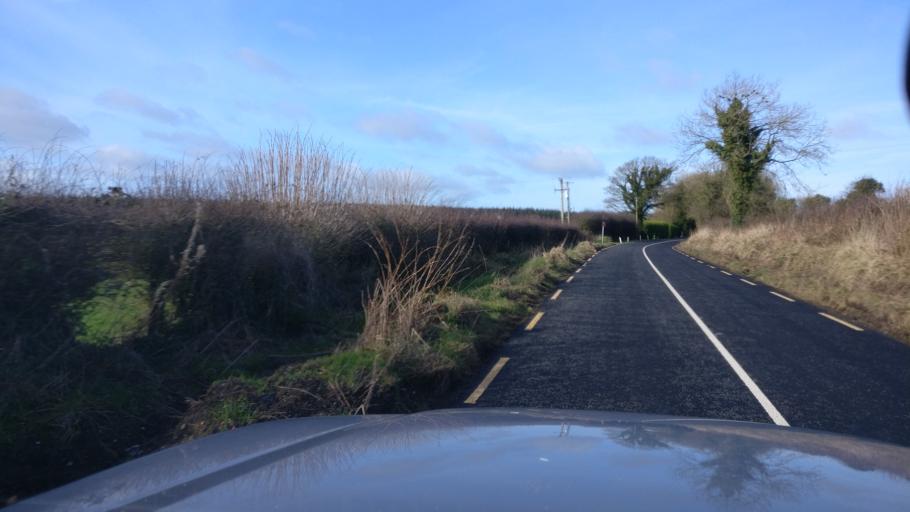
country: IE
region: Leinster
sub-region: Kilkenny
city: Castlecomer
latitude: 52.9059
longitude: -7.1823
